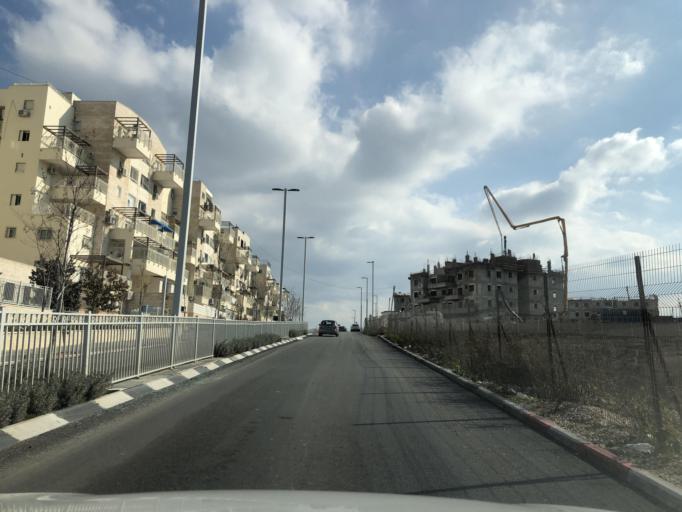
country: IL
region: Jerusalem
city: Modiin Ilit
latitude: 31.9347
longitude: 35.0517
